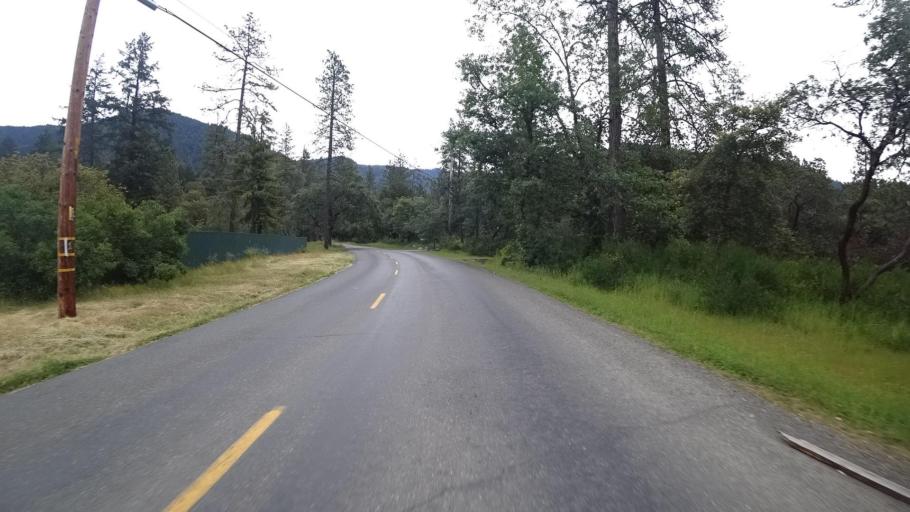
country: US
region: California
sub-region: Humboldt County
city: Willow Creek
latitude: 40.9472
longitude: -123.6287
